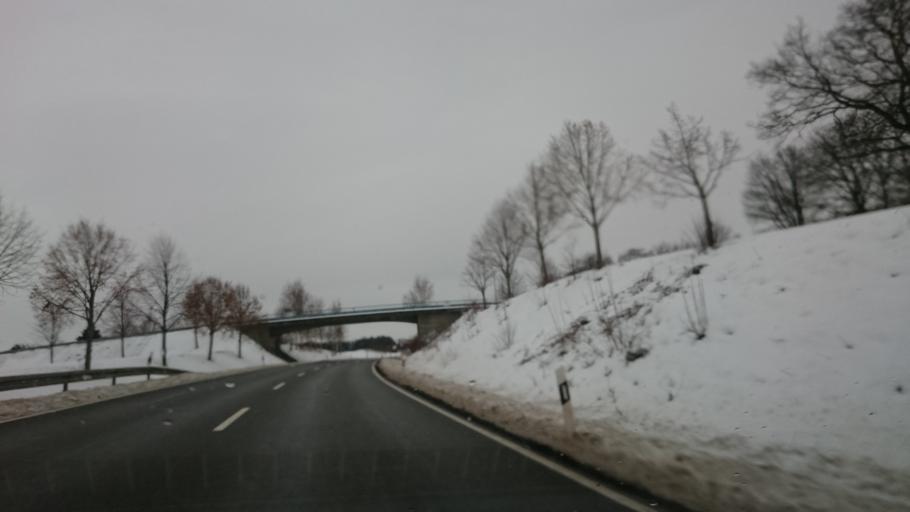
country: DE
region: Saxony
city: Lichtenstein
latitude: 50.7622
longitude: 12.6146
